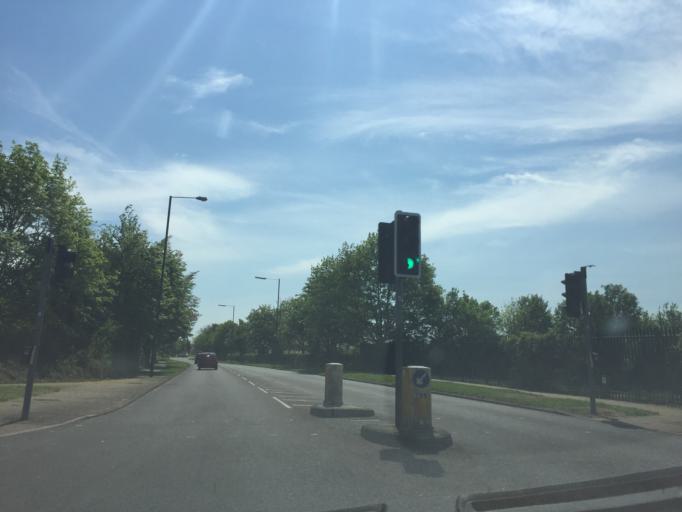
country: GB
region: England
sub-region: Essex
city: Harlow
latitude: 51.7578
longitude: 0.0894
